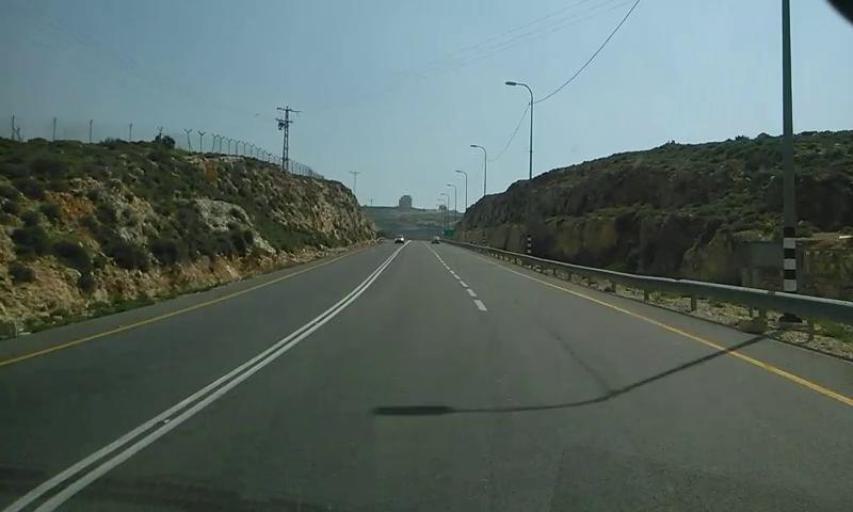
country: PS
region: West Bank
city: Jaba`
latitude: 31.8677
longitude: 35.2584
